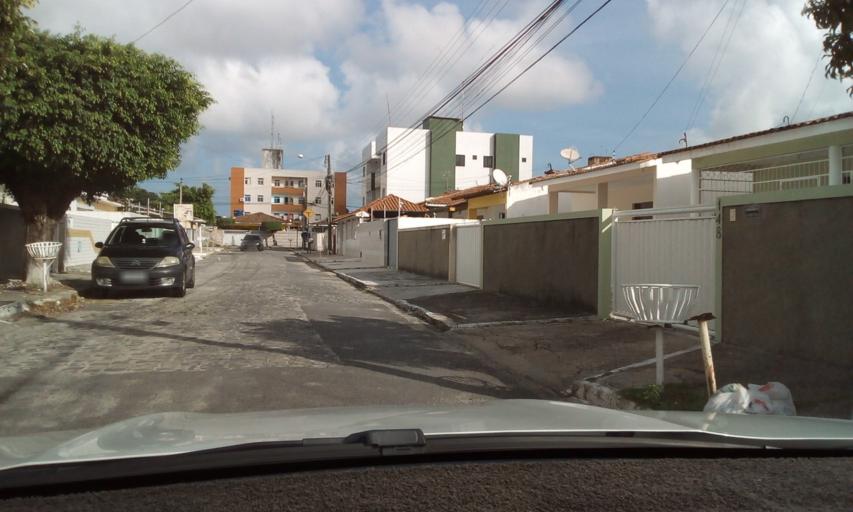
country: BR
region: Paraiba
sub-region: Joao Pessoa
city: Joao Pessoa
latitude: -7.1675
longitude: -34.8612
